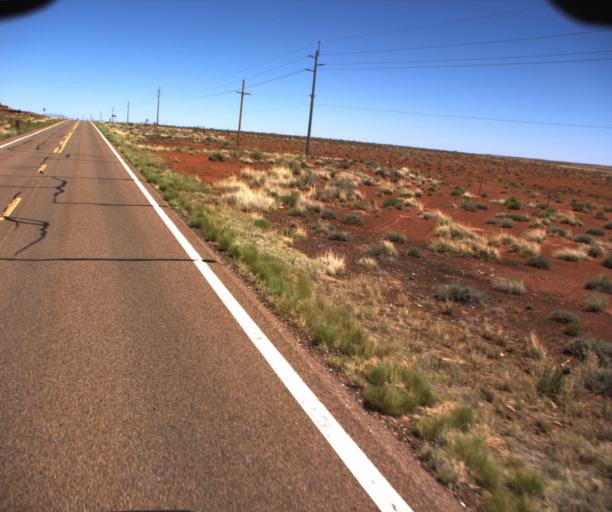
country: US
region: Arizona
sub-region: Coconino County
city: LeChee
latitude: 34.9280
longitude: -110.8033
